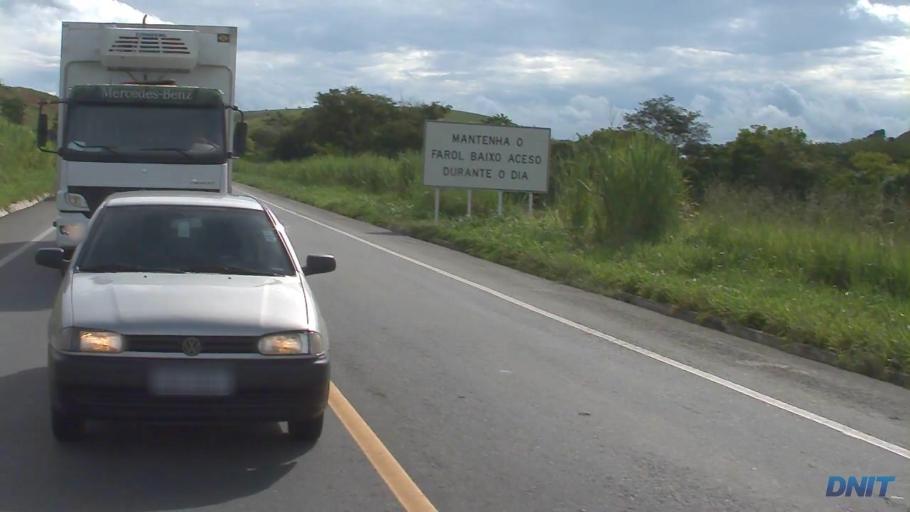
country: BR
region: Minas Gerais
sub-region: Belo Oriente
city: Belo Oriente
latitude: -19.2117
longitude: -42.3060
